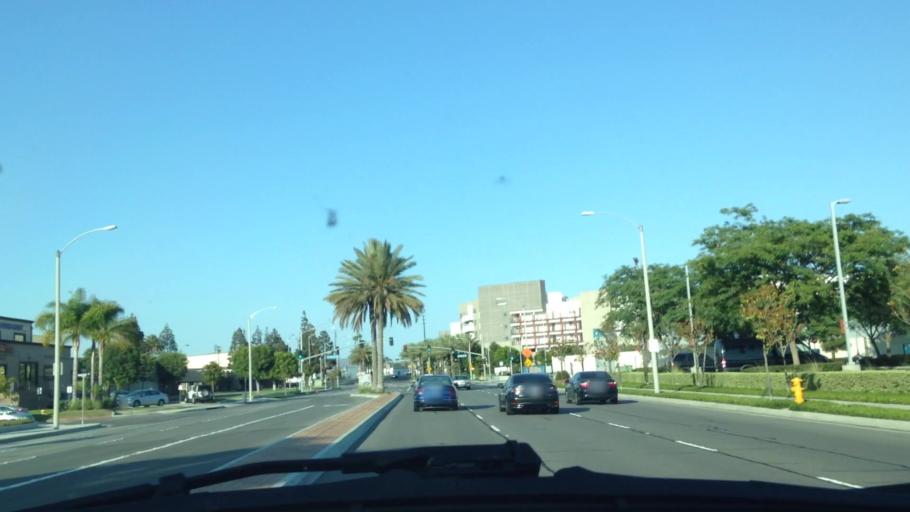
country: US
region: California
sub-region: Orange County
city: Placentia
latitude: 33.8544
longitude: -117.8442
